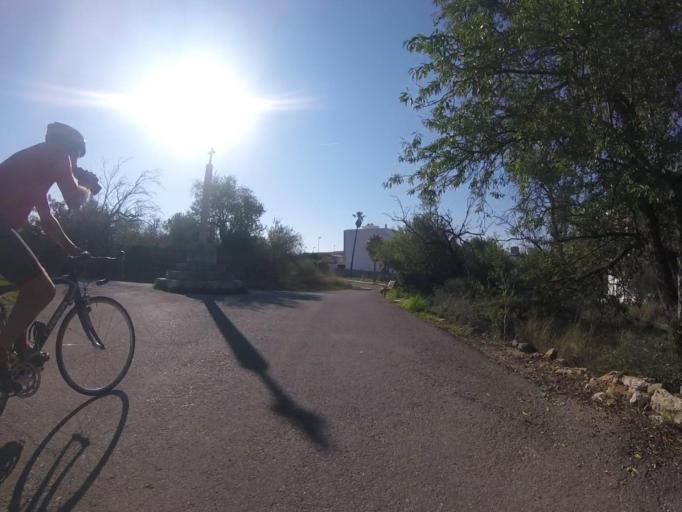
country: ES
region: Valencia
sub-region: Provincia de Castello
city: Cabanes
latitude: 40.1590
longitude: 0.0446
